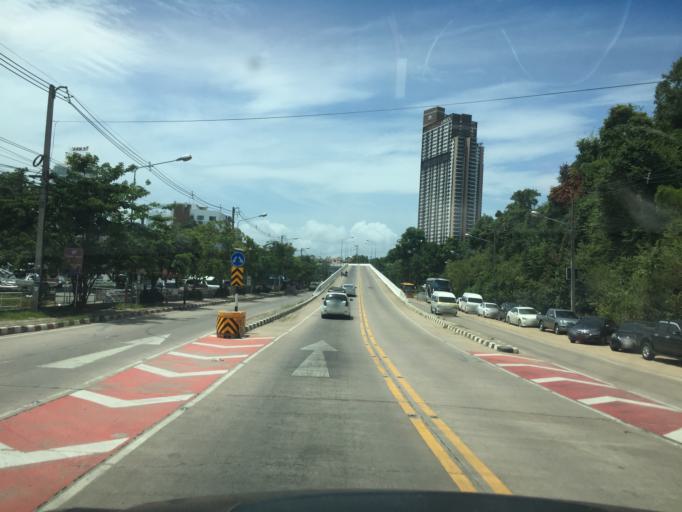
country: TH
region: Chon Buri
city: Phatthaya
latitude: 12.9230
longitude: 100.8678
